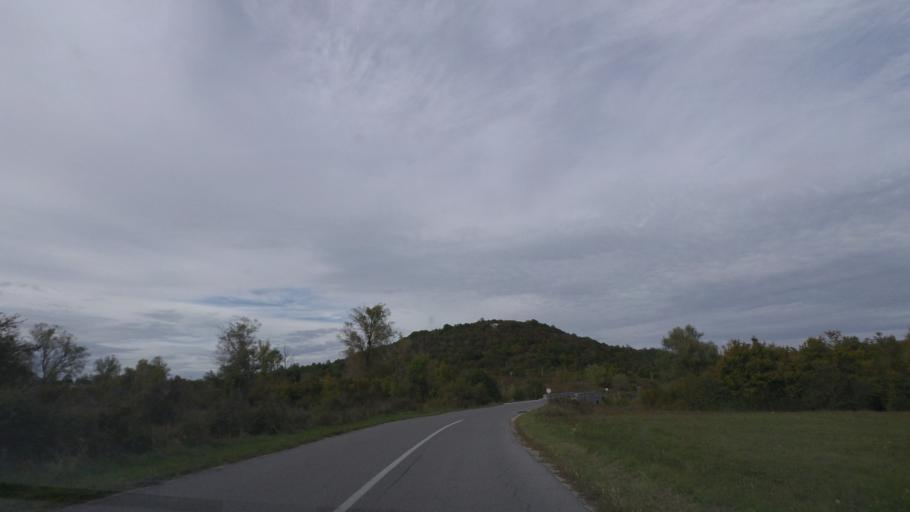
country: HR
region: Zadarska
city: Obrovac
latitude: 44.3781
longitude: 15.6730
